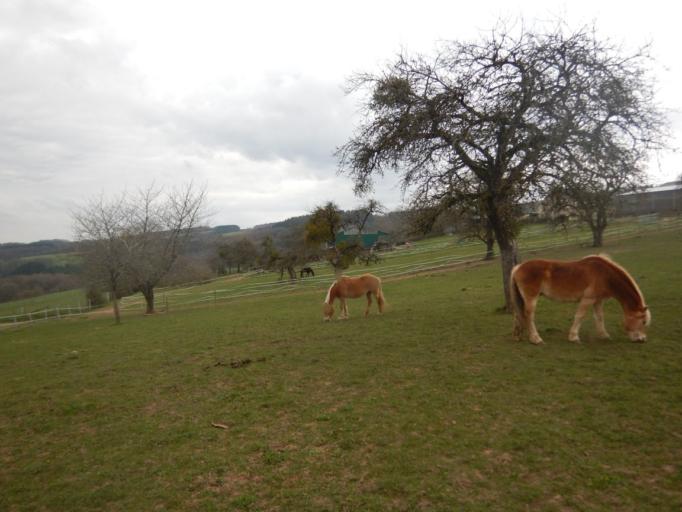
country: LU
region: Diekirch
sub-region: Canton de Redange
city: Ell
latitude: 49.7911
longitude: 5.8219
